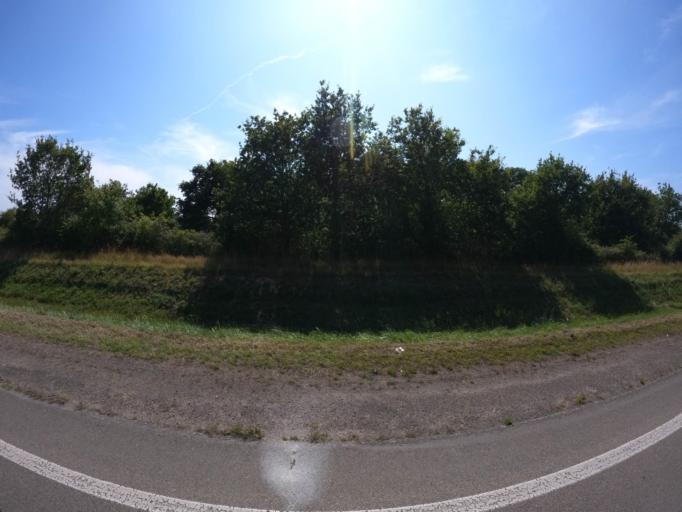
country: FR
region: Pays de la Loire
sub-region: Departement de la Loire-Atlantique
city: La Bernerie-en-Retz
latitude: 47.0915
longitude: -2.0337
